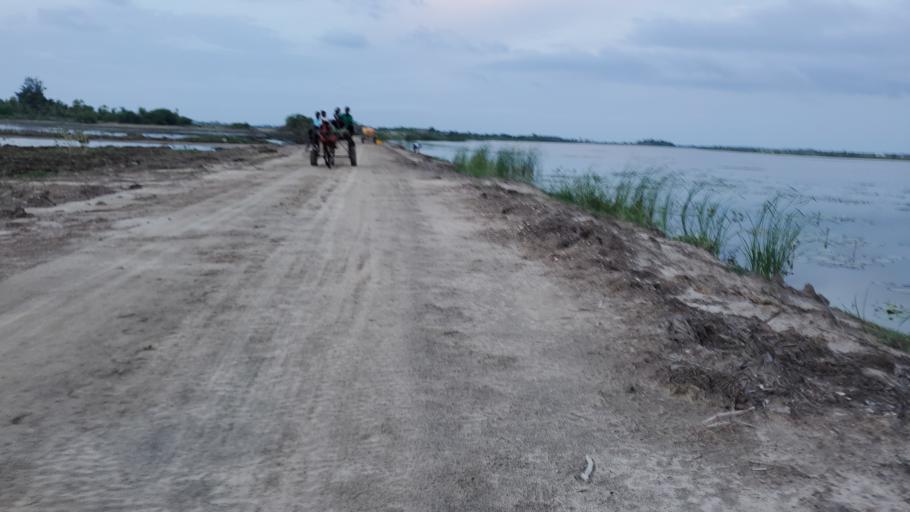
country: SN
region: Saint-Louis
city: Saint-Louis
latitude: 16.0406
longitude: -16.4169
